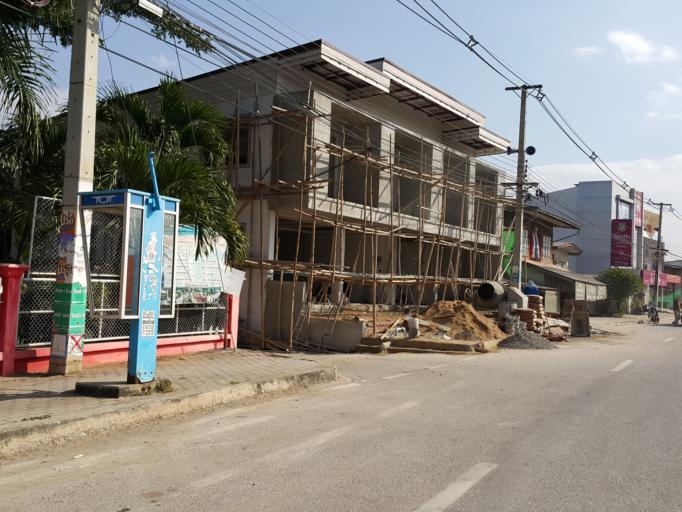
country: TH
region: Lamphun
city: Ban Hong
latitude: 18.2960
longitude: 98.8162
